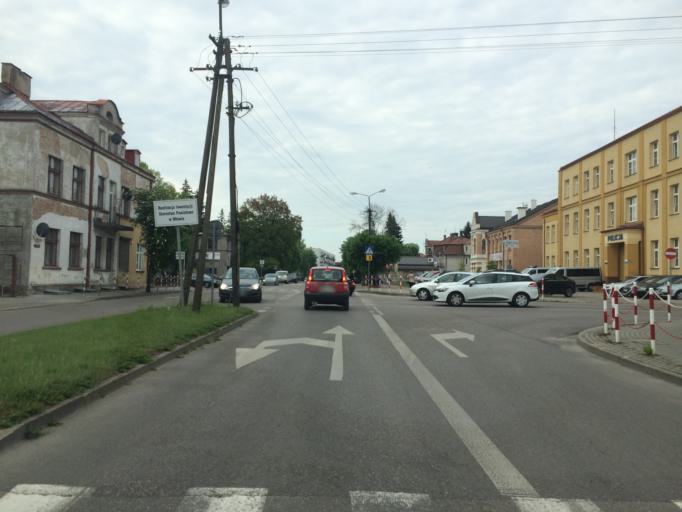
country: PL
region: Masovian Voivodeship
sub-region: Powiat mlawski
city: Mlawa
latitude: 53.1139
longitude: 20.3749
